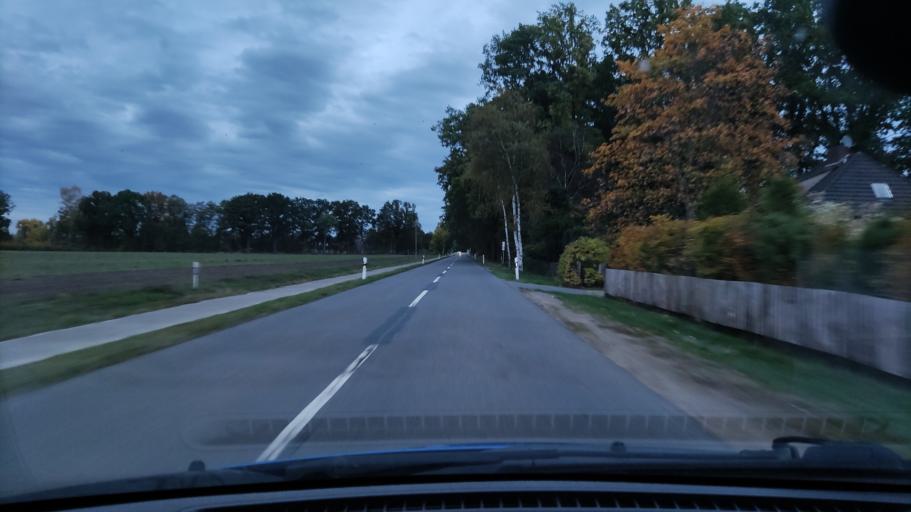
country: DE
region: Lower Saxony
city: Gorleben
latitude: 53.0418
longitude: 11.3853
